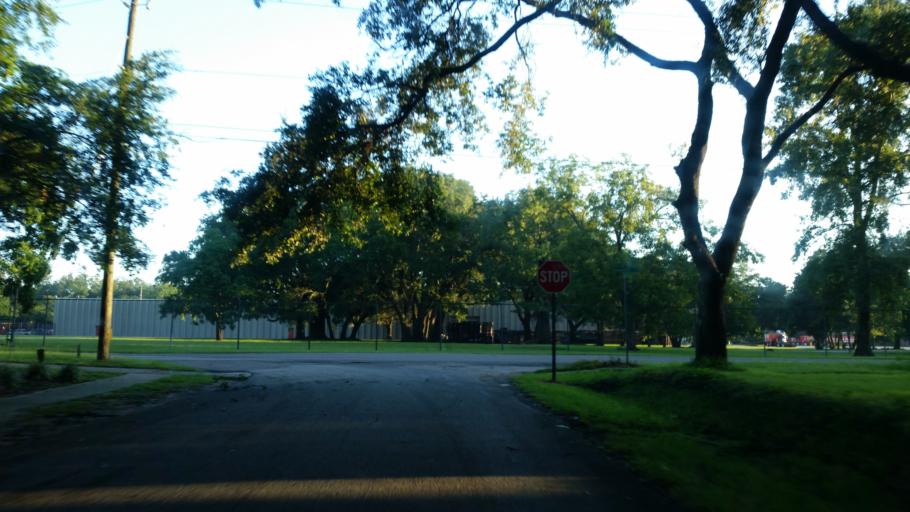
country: US
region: Florida
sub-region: Escambia County
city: Ferry Pass
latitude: 30.4992
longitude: -87.2175
